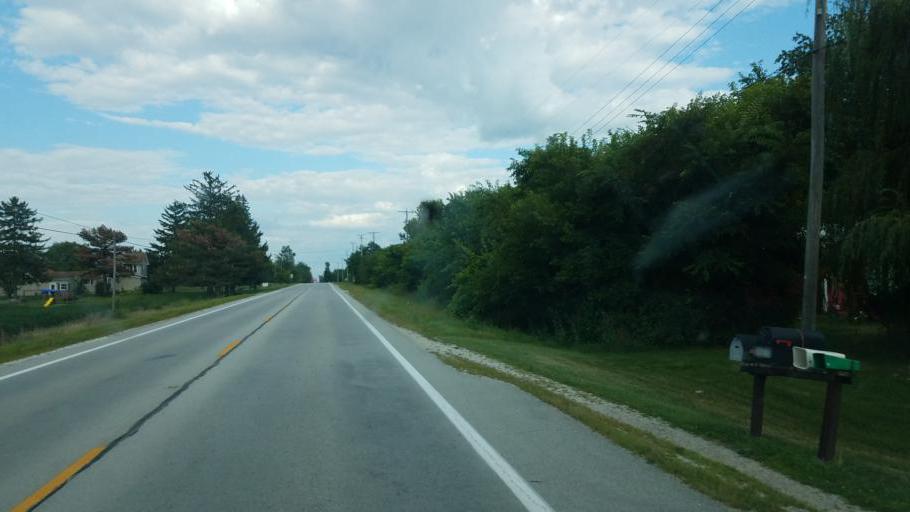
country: US
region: Ohio
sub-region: Sandusky County
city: Gibsonburg
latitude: 41.3410
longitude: -83.3334
